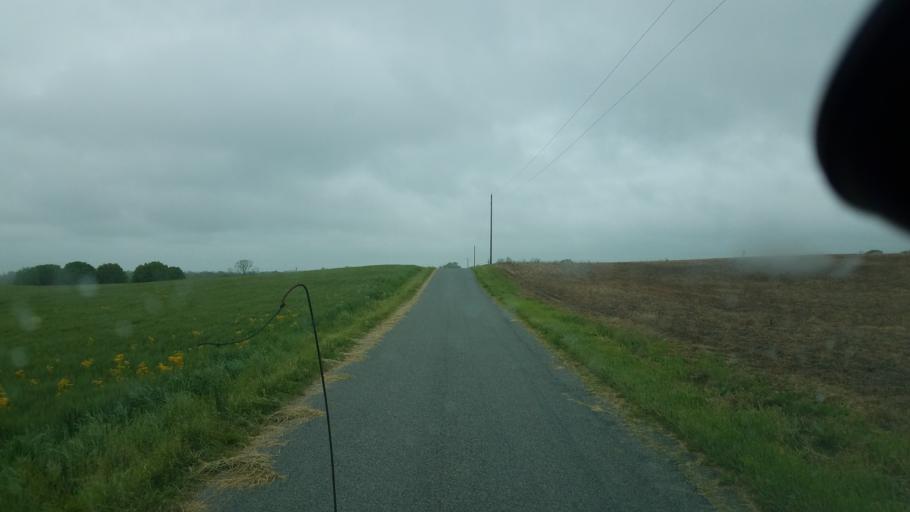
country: US
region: Ohio
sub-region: Highland County
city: Greenfield
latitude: 39.3327
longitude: -83.4563
